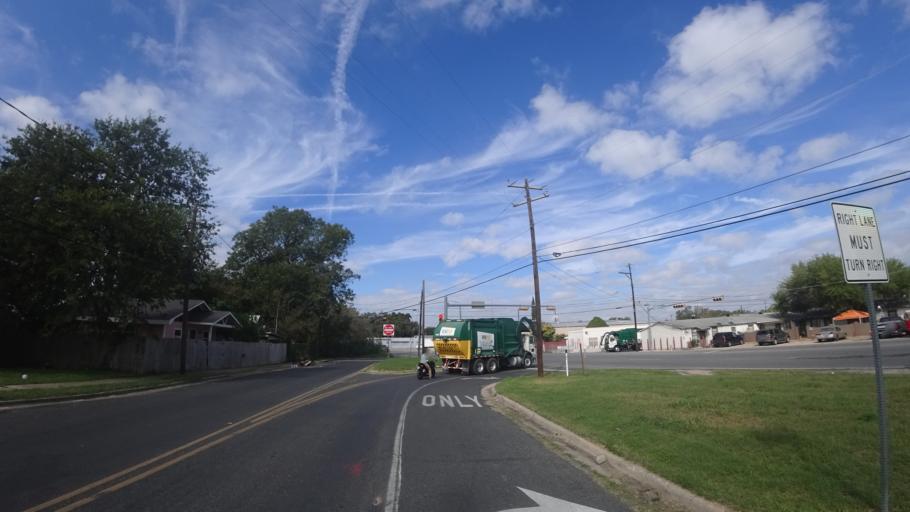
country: US
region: Texas
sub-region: Travis County
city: Austin
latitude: 30.2516
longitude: -97.7038
